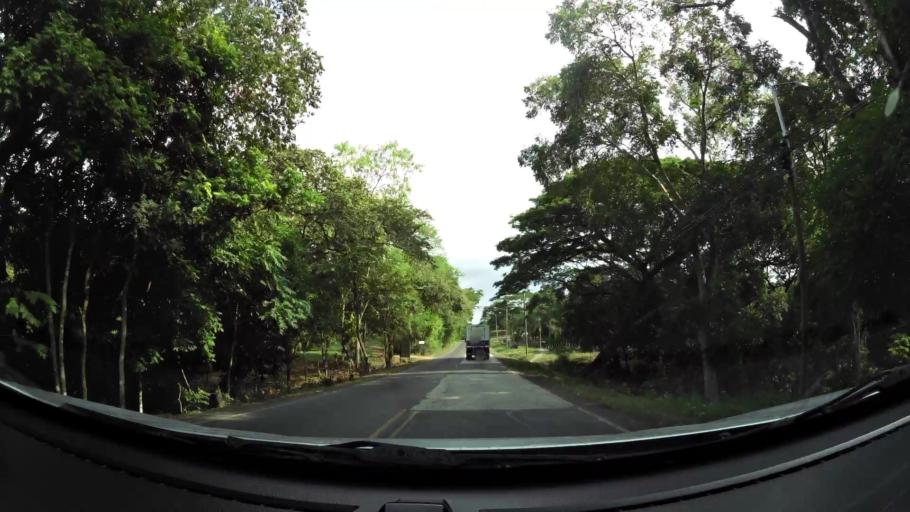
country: CR
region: Guanacaste
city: Juntas
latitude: 10.1758
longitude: -84.9284
